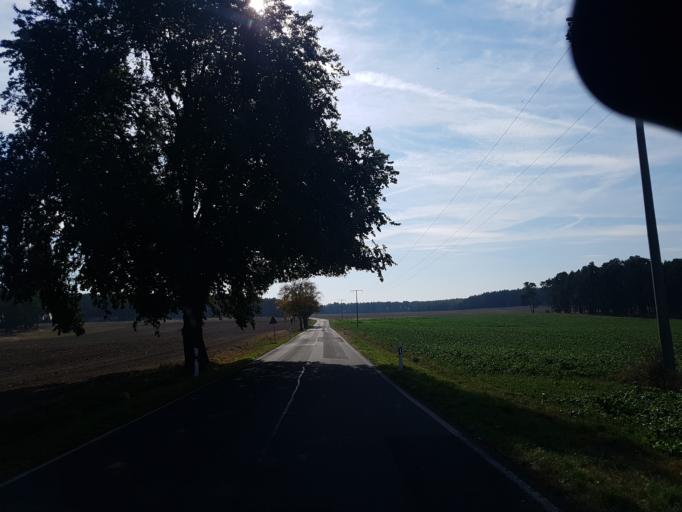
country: DE
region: Brandenburg
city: Hohenbucko
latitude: 51.7231
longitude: 13.4931
